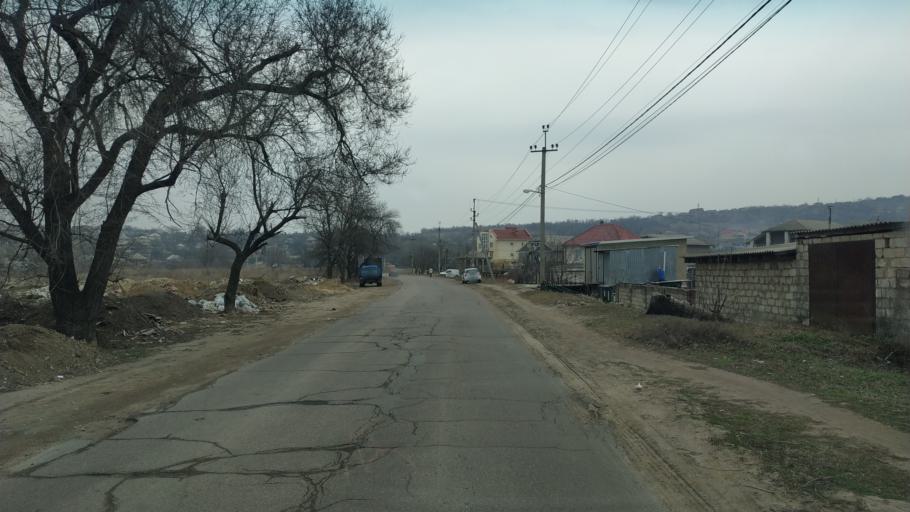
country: MD
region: Chisinau
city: Singera
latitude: 46.9179
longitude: 28.9767
